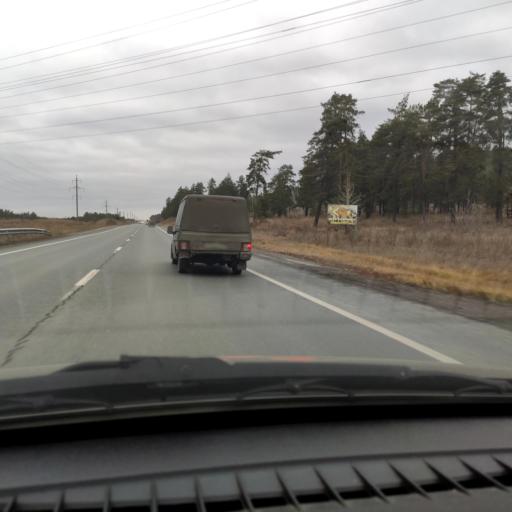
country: RU
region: Samara
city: Volzhskiy
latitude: 53.4484
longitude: 50.0966
